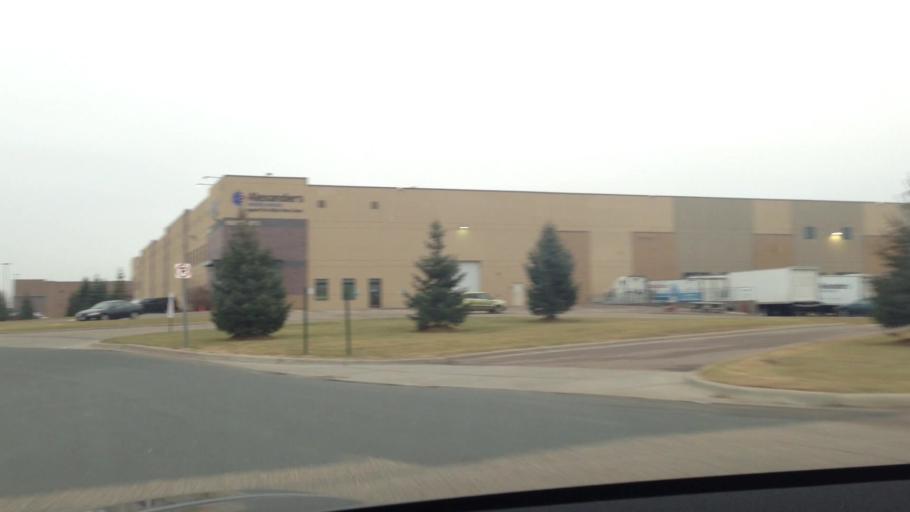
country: US
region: Minnesota
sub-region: Dakota County
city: Mendota Heights
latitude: 44.8548
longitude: -93.1368
